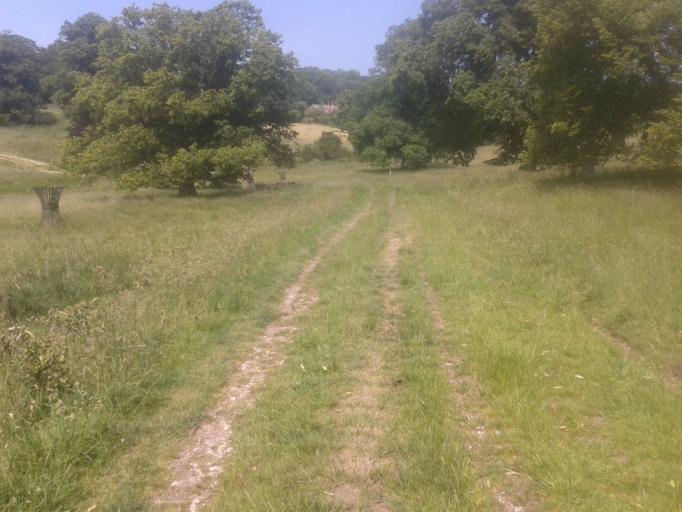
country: GB
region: England
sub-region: East Riding of Yorkshire
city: Londesborough
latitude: 53.8962
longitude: -0.6736
